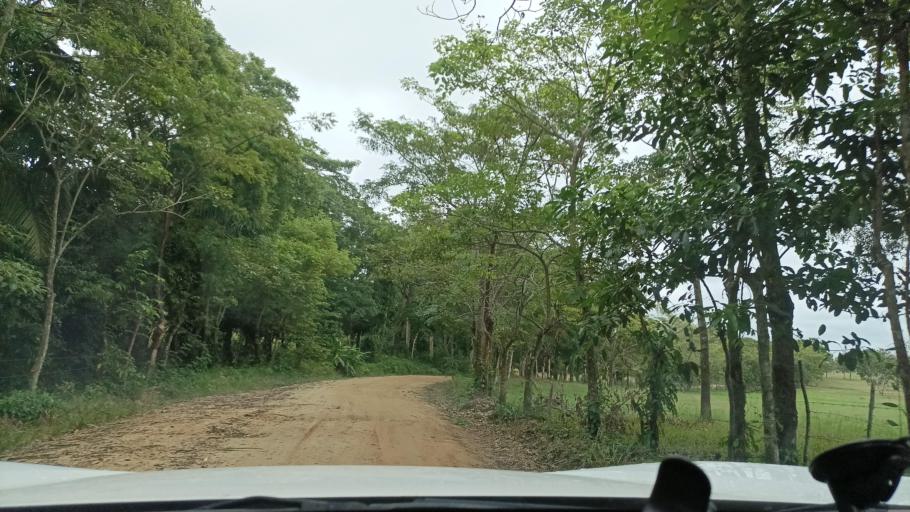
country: MX
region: Veracruz
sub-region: Moloacan
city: Cuichapa
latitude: 17.7955
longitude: -94.3744
